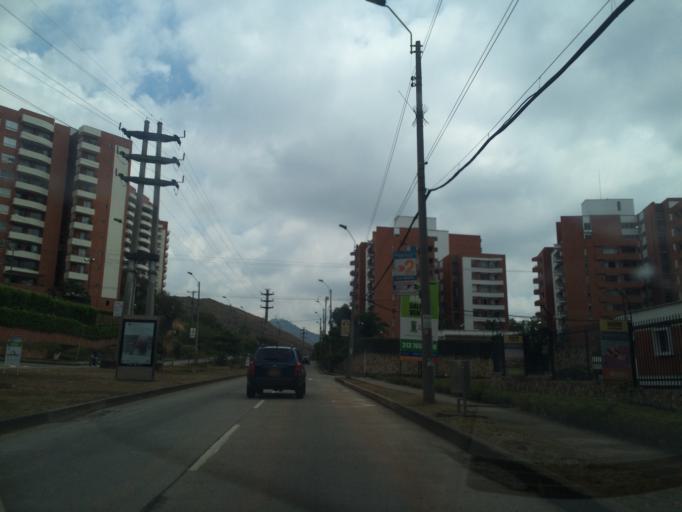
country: CO
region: Valle del Cauca
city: Cali
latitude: 3.4305
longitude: -76.5514
